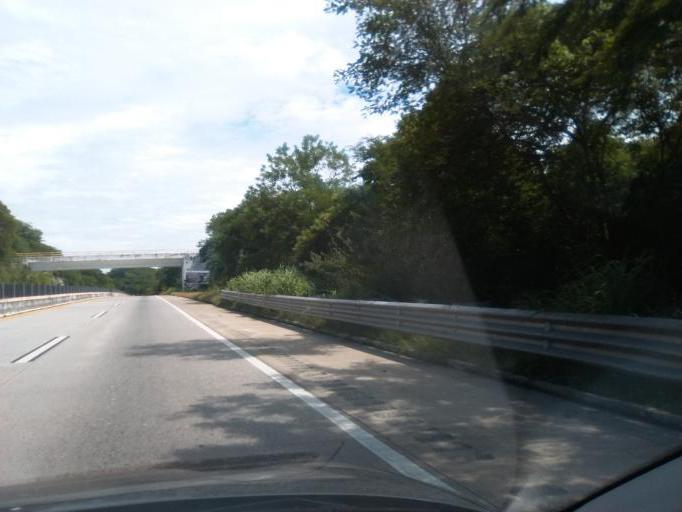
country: MX
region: Guerrero
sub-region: Acapulco de Juarez
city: Pueblo Madero (El Playon)
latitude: 17.0747
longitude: -99.6136
